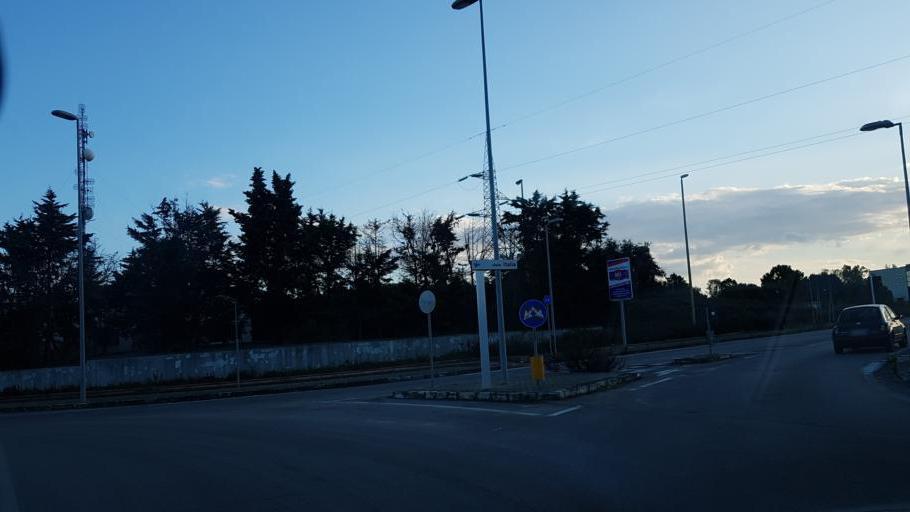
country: IT
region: Apulia
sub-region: Provincia di Lecce
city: Surbo
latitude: 40.3801
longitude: 18.1251
